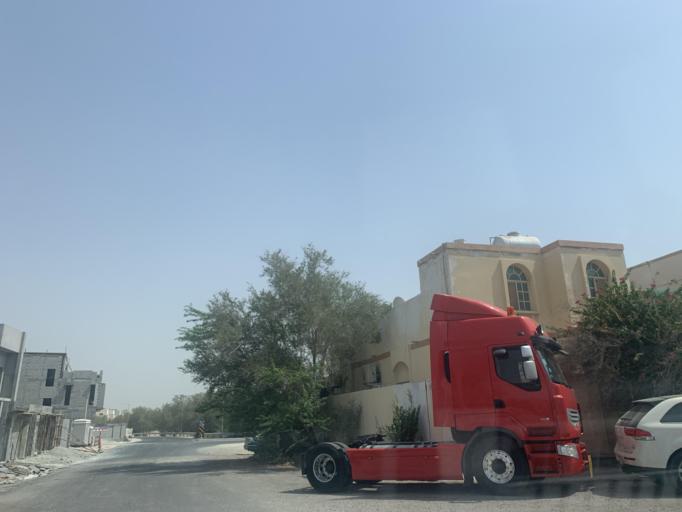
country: BH
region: Northern
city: Madinat `Isa
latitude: 26.1914
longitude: 50.4895
